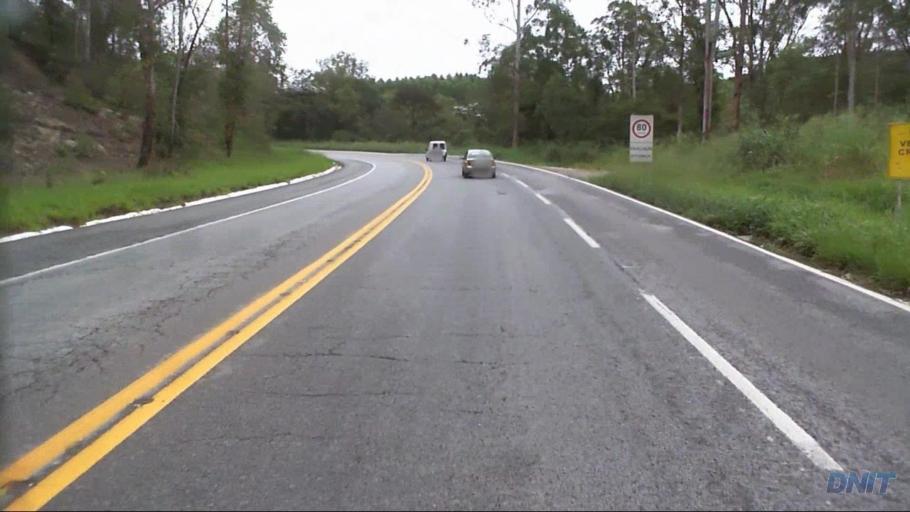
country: BR
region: Minas Gerais
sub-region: Joao Monlevade
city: Joao Monlevade
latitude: -19.8511
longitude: -43.2729
